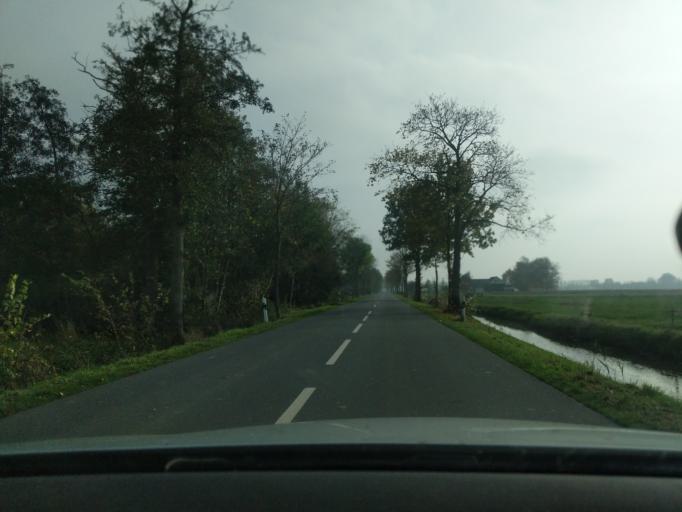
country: DE
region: Lower Saxony
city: Ihlienworth
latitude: 53.7385
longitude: 8.9316
